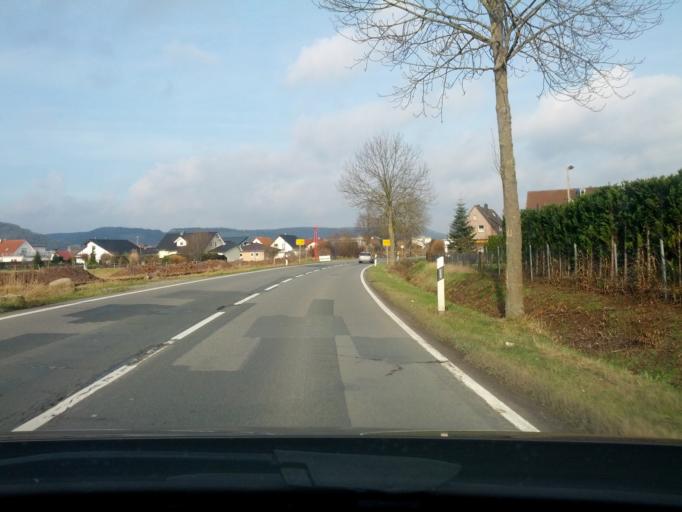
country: DE
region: North Rhine-Westphalia
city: Beverungen
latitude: 51.6538
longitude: 9.3871
